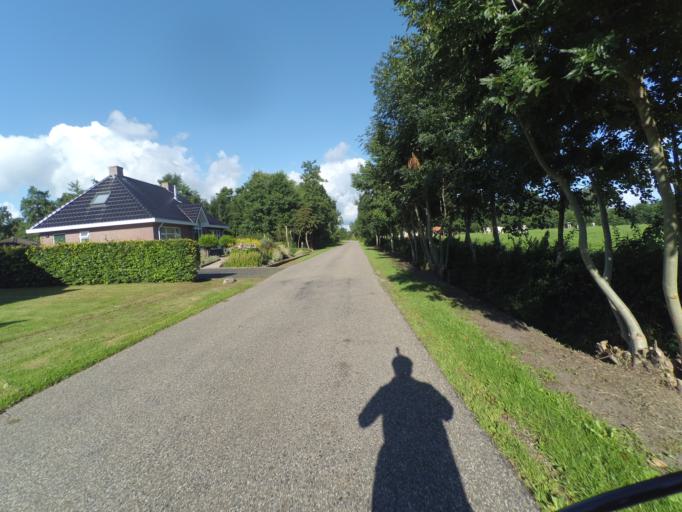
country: NL
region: Friesland
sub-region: Gemeente Kollumerland en Nieuwkruisland
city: Kollumerzwaag
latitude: 53.2743
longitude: 6.1006
